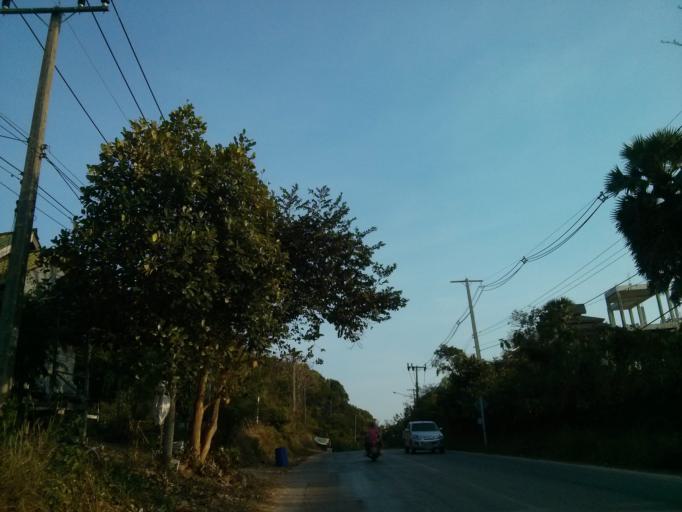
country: TH
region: Krabi
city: Saladan
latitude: 7.5598
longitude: 99.0386
